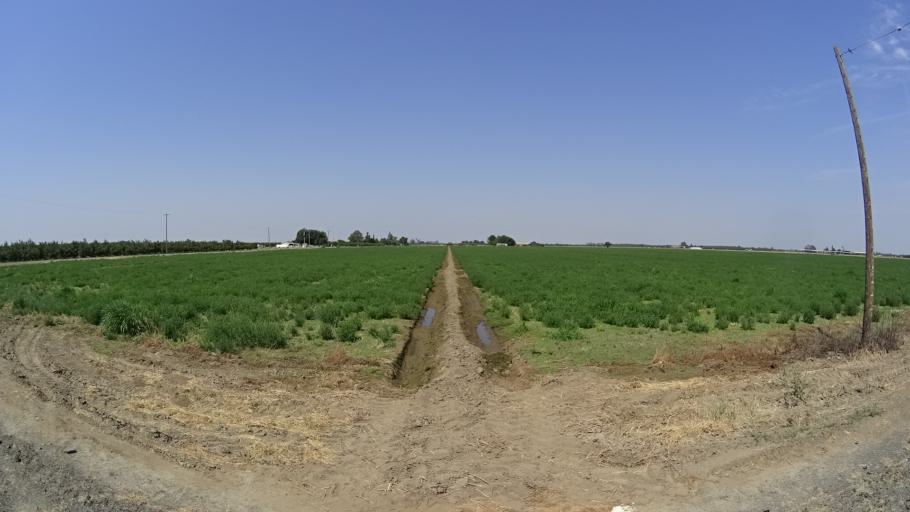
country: US
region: California
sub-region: Kings County
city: Armona
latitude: 36.3288
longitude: -119.7448
